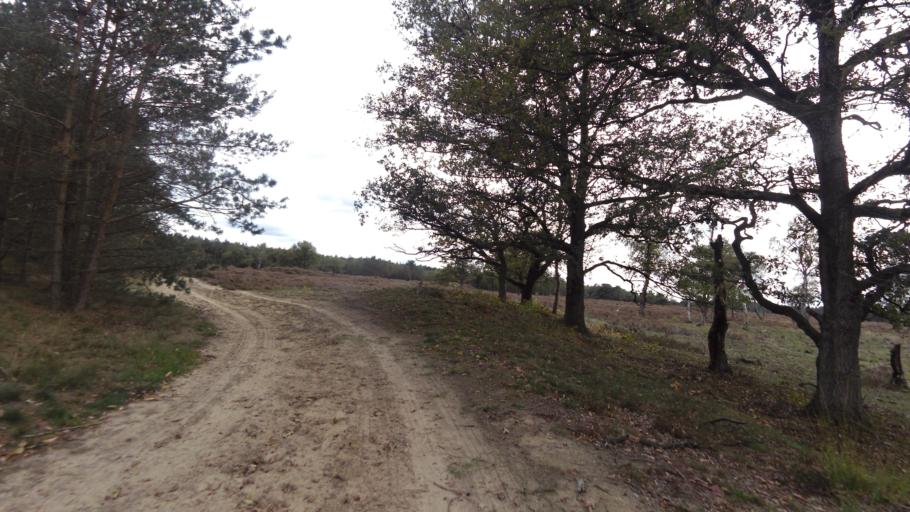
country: NL
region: Gelderland
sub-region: Gemeente Barneveld
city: Stroe
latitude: 52.1791
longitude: 5.7246
